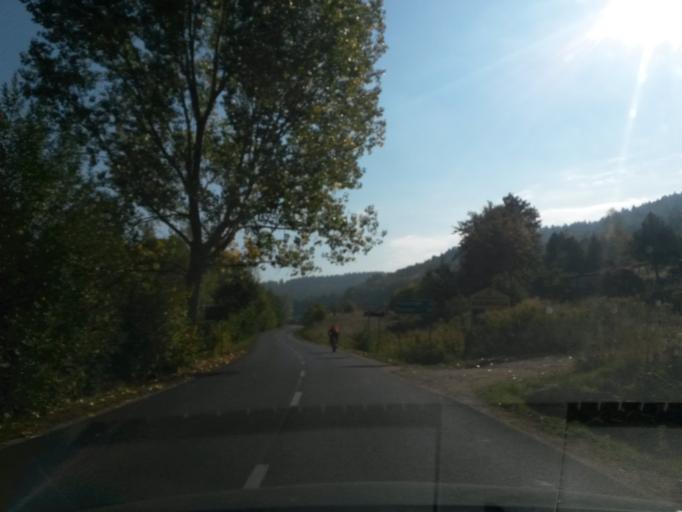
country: PL
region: Lower Silesian Voivodeship
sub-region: Powiat jeleniogorski
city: Piechowice
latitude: 50.8460
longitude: 15.6122
